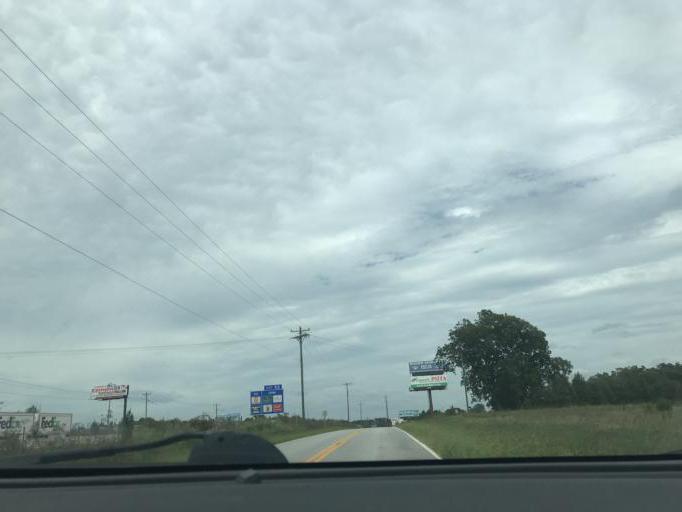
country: US
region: South Carolina
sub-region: Cherokee County
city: Gaffney
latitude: 35.0899
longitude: -81.6922
